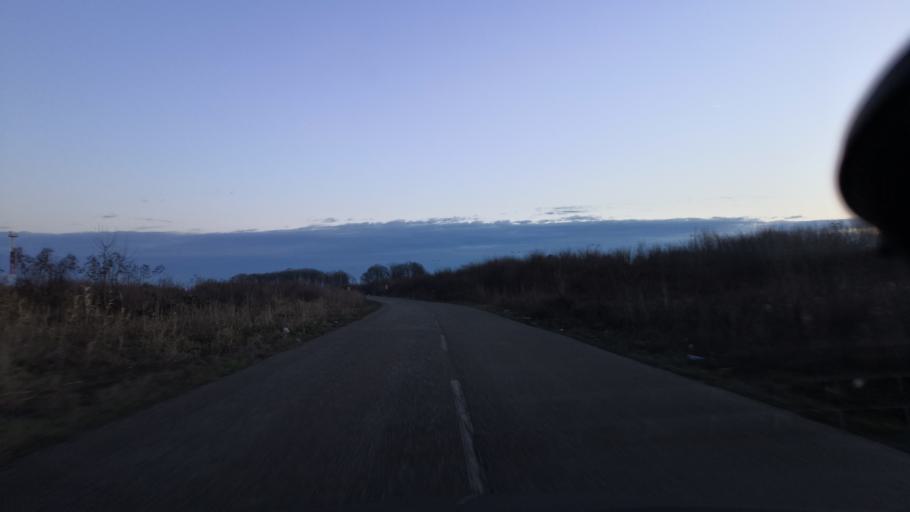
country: RS
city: Simanovci
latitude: 44.8823
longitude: 20.1179
